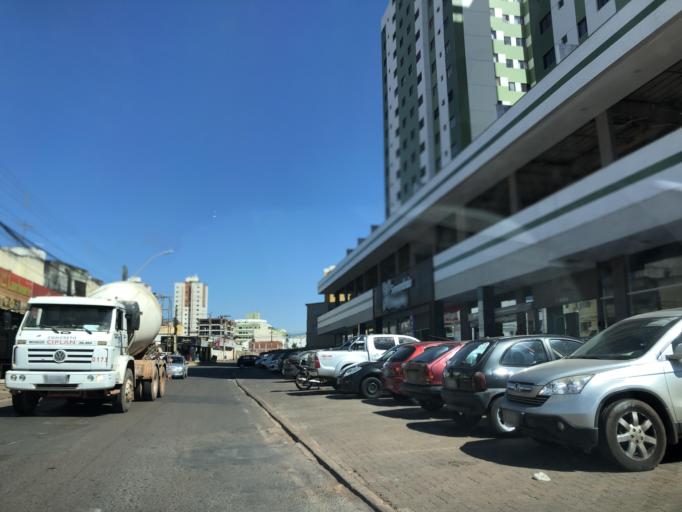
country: BR
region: Federal District
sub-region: Brasilia
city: Brasilia
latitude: -15.8648
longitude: -48.0574
